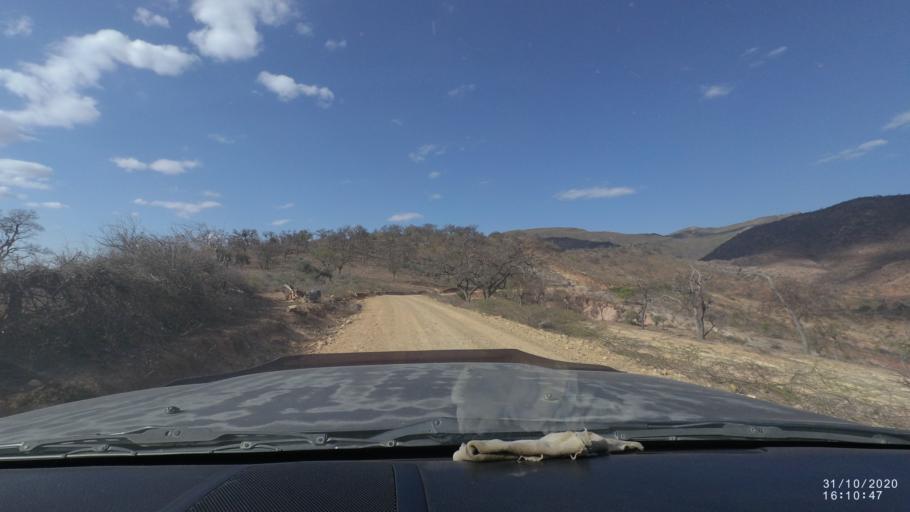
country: BO
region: Chuquisaca
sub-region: Provincia Zudanez
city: Mojocoya
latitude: -18.3824
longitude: -64.6272
